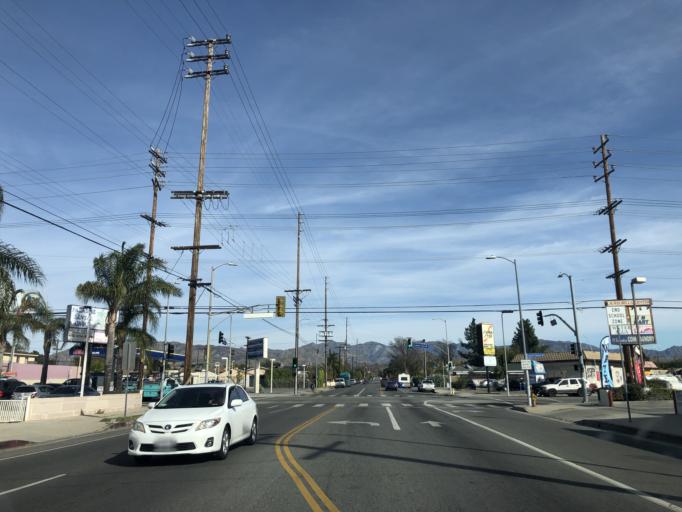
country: US
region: California
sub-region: Los Angeles County
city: San Fernando
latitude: 34.2524
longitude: -118.4262
